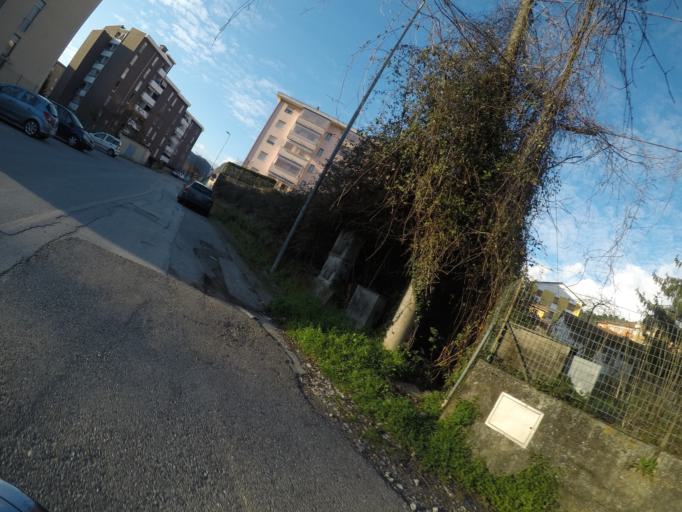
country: IT
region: Tuscany
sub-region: Provincia di Massa-Carrara
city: Carrara
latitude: 44.0571
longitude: 10.0895
